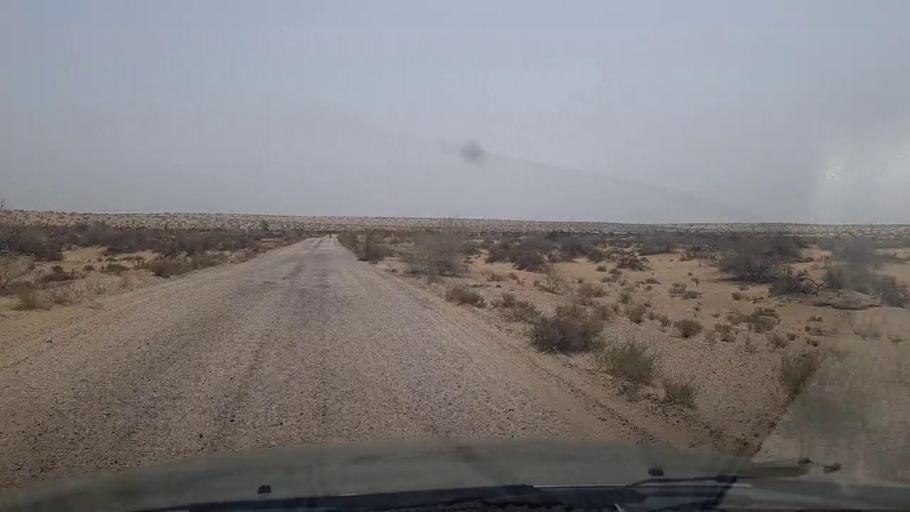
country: PK
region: Sindh
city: Bozdar
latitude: 27.0126
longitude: 68.7916
